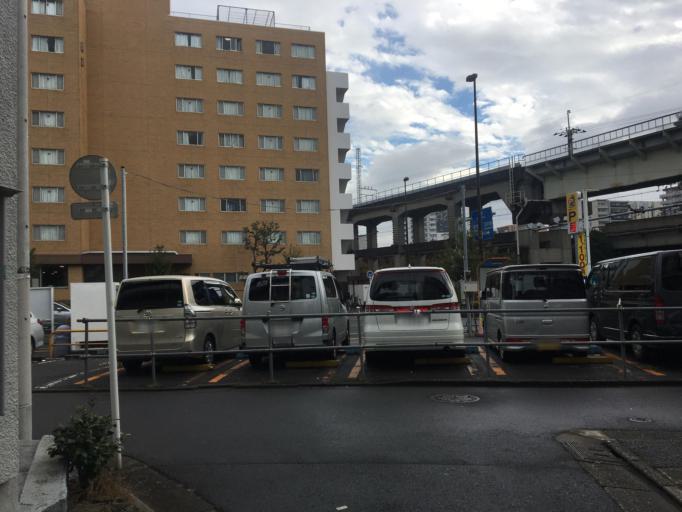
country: JP
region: Tokyo
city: Urayasu
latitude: 35.6984
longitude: 139.8335
